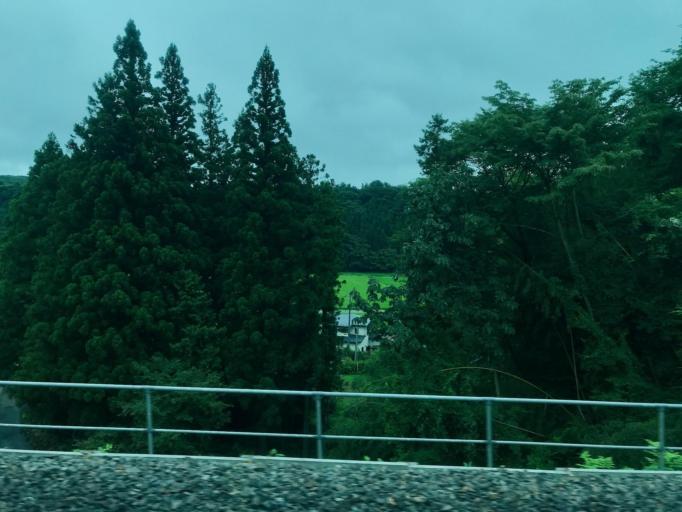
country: JP
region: Tochigi
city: Kuroiso
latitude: 37.0587
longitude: 140.1589
